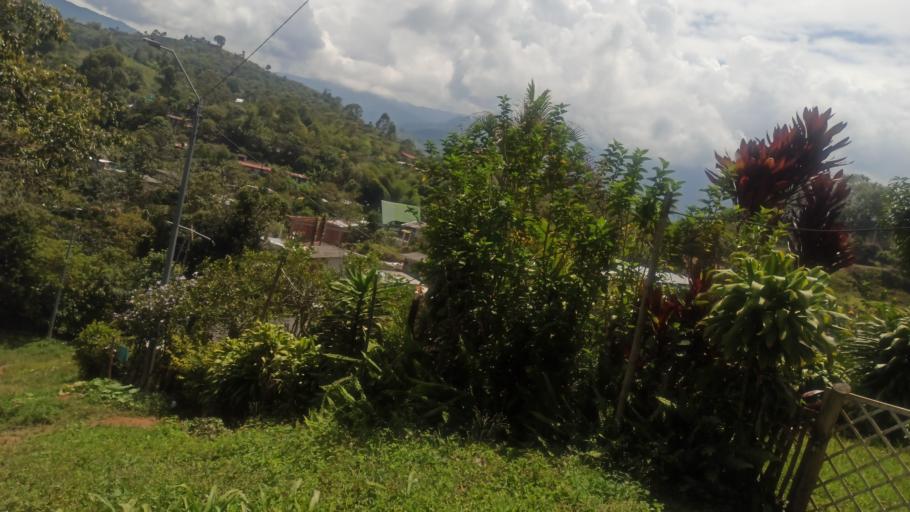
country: CO
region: Valle del Cauca
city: Jamundi
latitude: 3.2093
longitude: -76.6540
